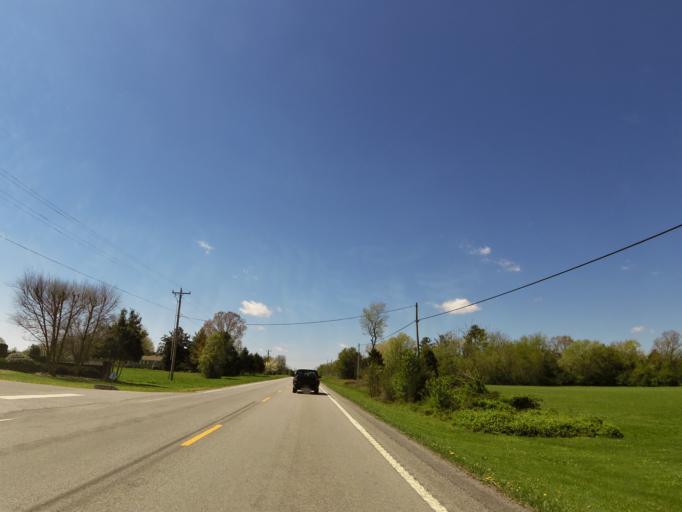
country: US
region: Tennessee
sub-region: DeKalb County
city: Smithville
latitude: 35.9552
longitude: -85.7721
